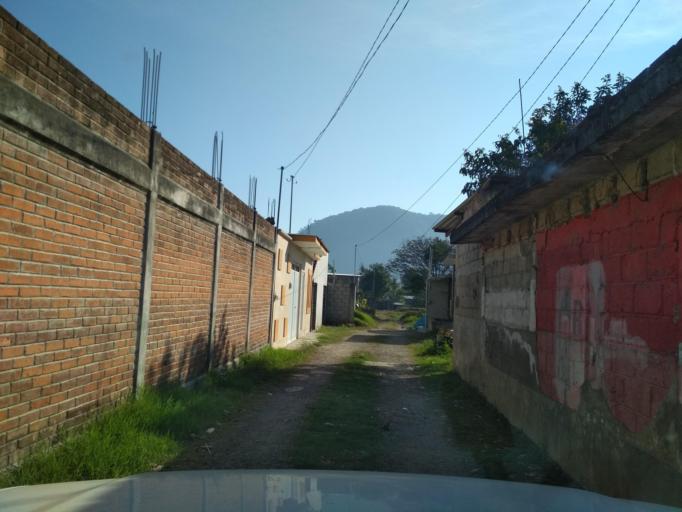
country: MX
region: Veracruz
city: Jalapilla
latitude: 18.8228
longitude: -97.0837
